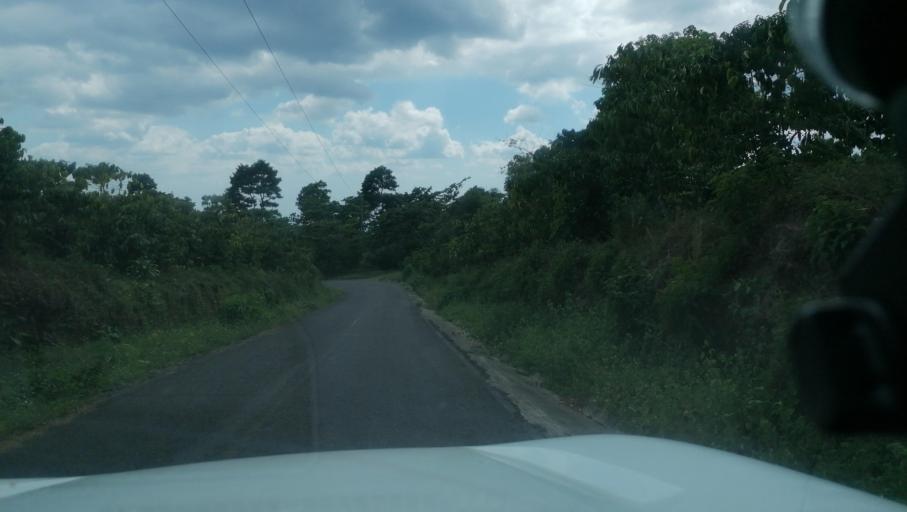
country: MX
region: Chiapas
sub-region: Cacahoatan
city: Benito Juarez
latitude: 15.0515
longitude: -92.1525
